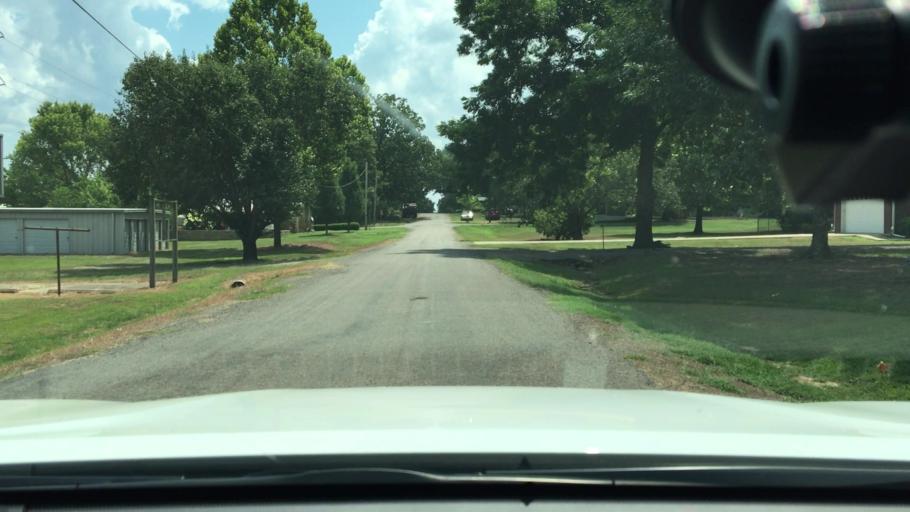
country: US
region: Arkansas
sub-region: Logan County
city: Paris
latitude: 35.2925
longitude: -93.6371
